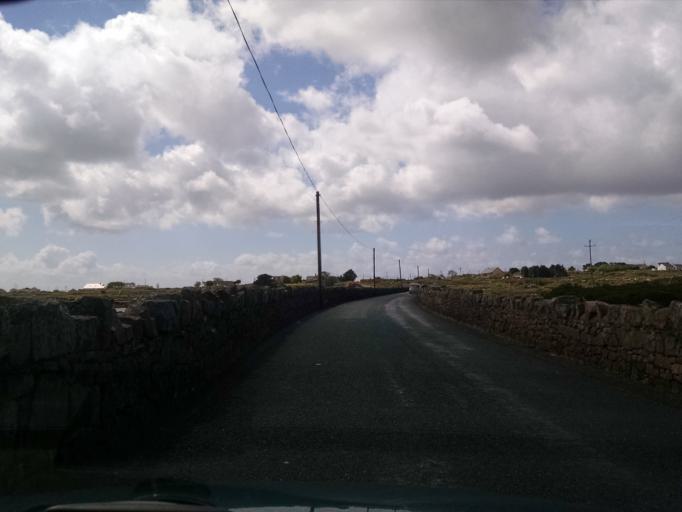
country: IE
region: Connaught
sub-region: County Galway
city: Oughterard
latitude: 53.3038
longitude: -9.6353
